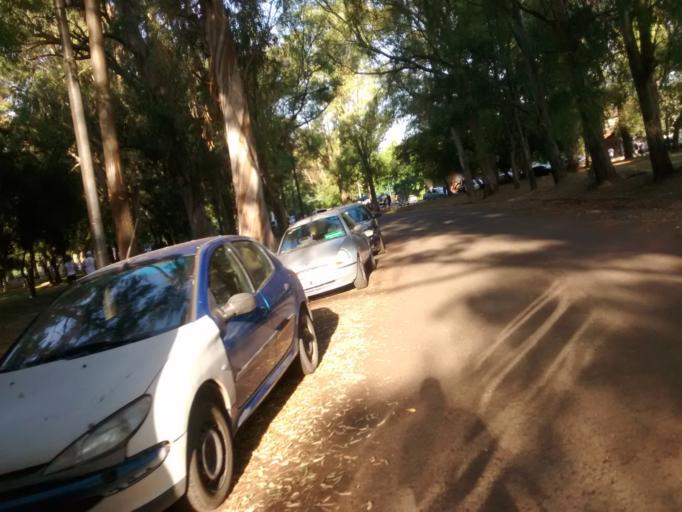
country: AR
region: Buenos Aires
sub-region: Partido de La Plata
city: La Plata
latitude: -34.9135
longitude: -57.9346
